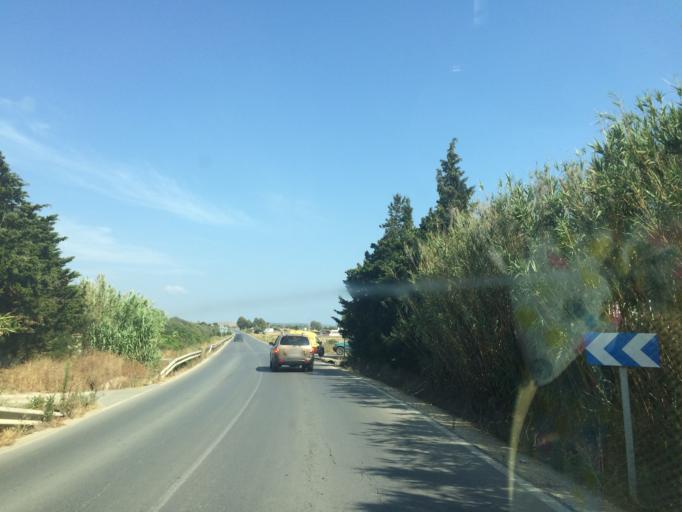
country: ES
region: Andalusia
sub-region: Provincia de Cadiz
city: Conil de la Frontera
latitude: 36.2417
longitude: -6.0605
